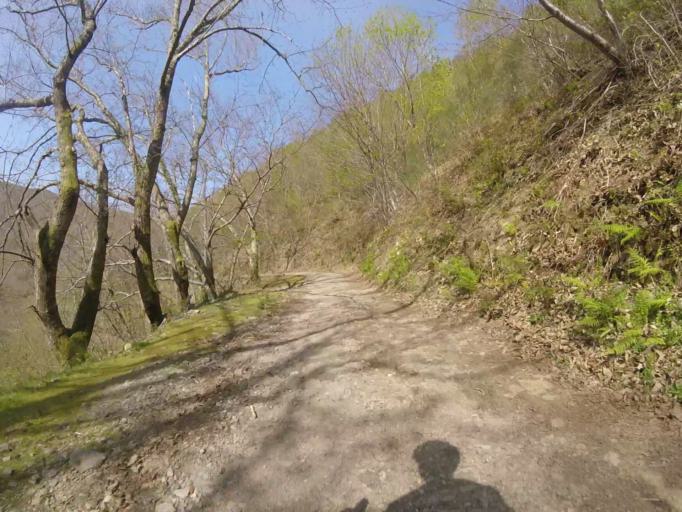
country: ES
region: Basque Country
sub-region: Provincia de Guipuzcoa
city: Irun
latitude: 43.2663
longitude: -1.8065
